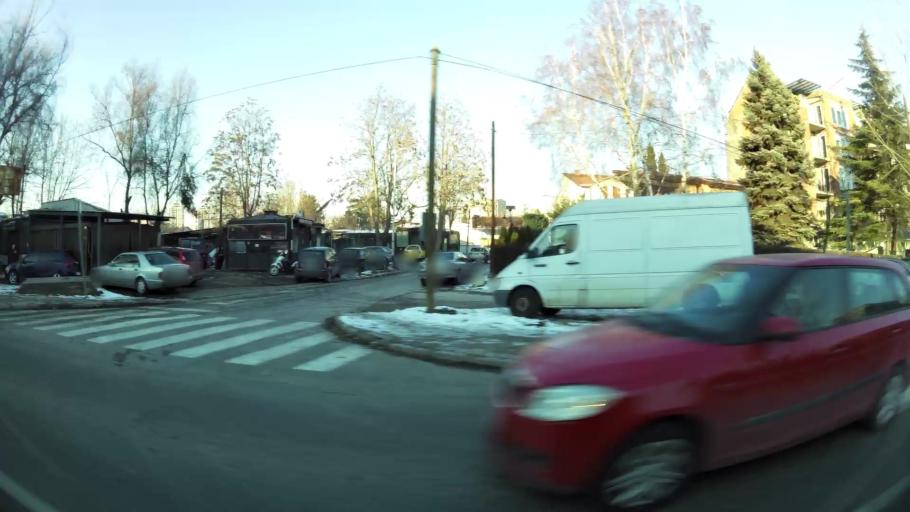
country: MK
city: Krushopek
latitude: 41.9993
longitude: 21.3833
